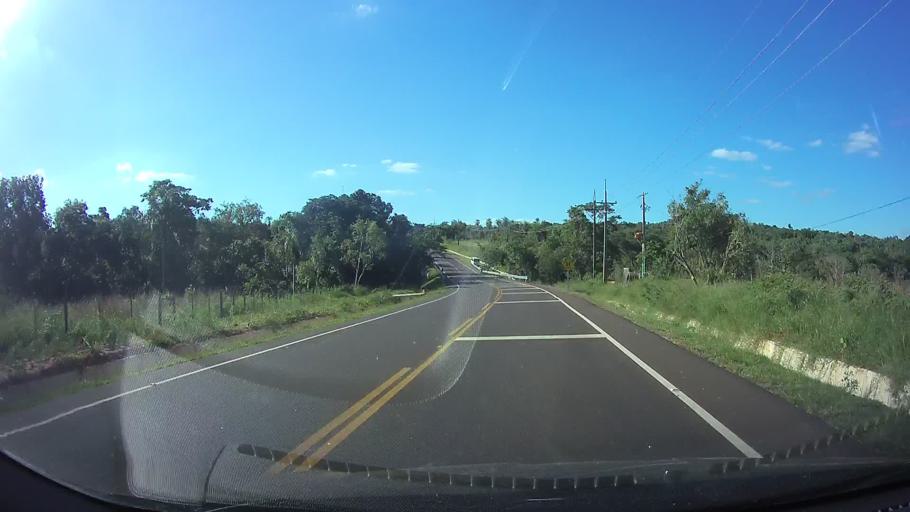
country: PY
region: Cordillera
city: Caacupe
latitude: -25.3550
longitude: -57.1478
